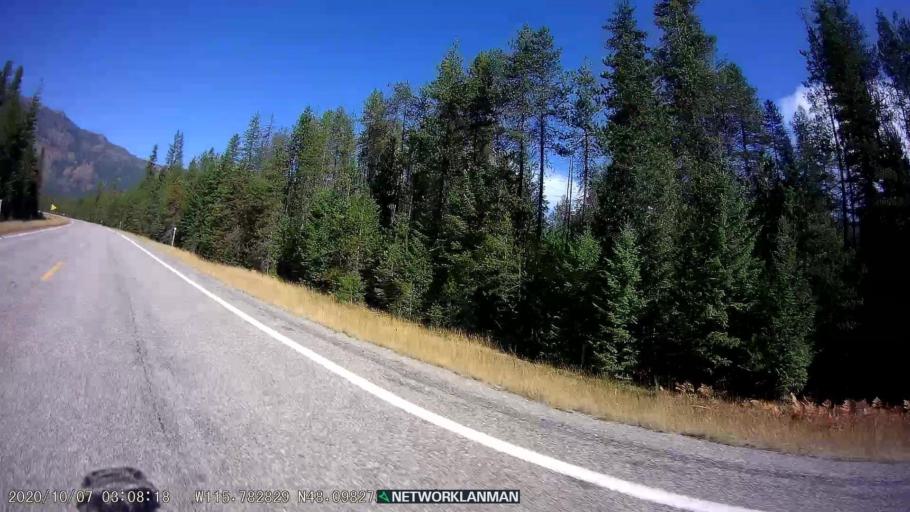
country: US
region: Montana
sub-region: Lincoln County
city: Libby
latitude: 48.0987
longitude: -115.7829
